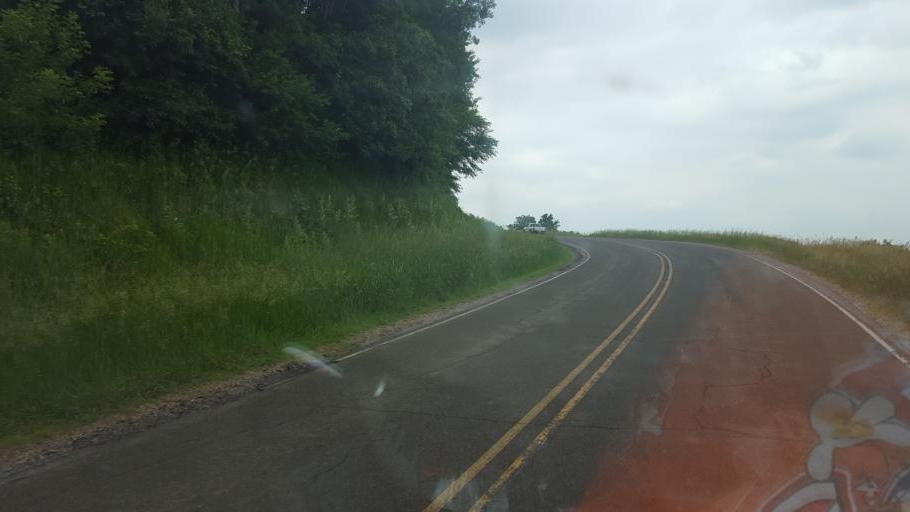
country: US
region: Wisconsin
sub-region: Vernon County
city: Hillsboro
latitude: 43.6429
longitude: -90.2855
